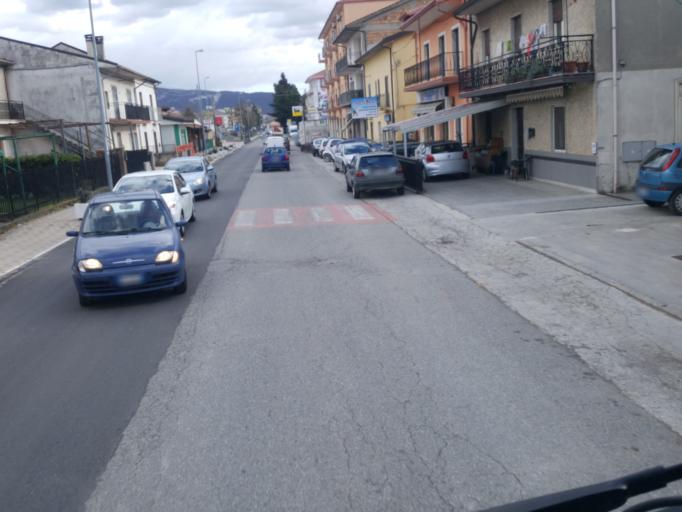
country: IT
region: Calabria
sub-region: Provincia di Cosenza
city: Santo Stefano di Rogliano
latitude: 39.2036
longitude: 16.3122
